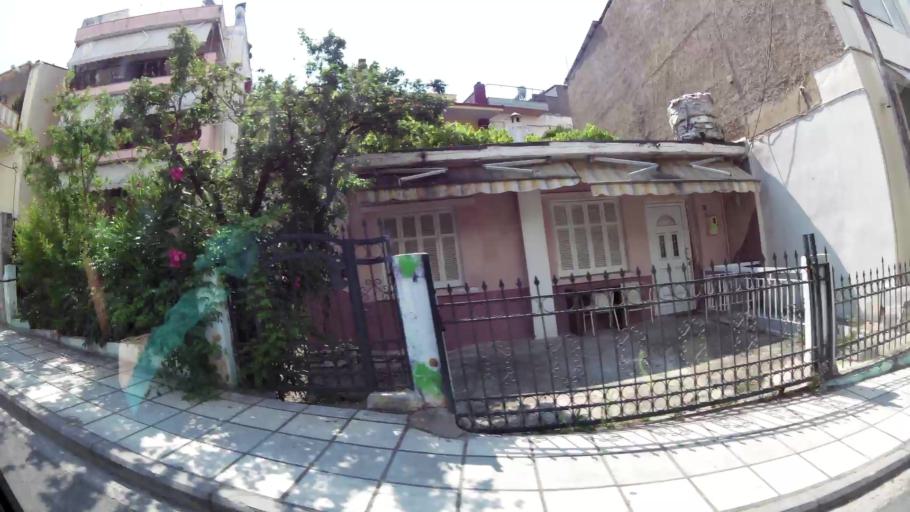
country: GR
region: Central Macedonia
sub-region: Nomos Thessalonikis
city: Polichni
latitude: 40.6651
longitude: 22.9470
